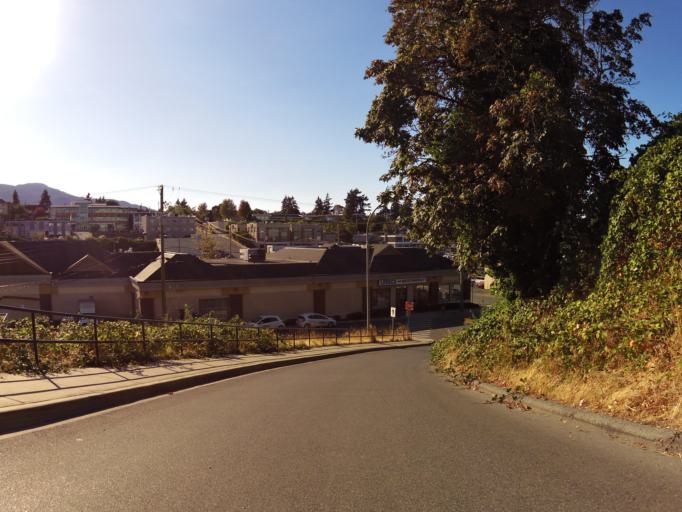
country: CA
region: British Columbia
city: Nanaimo
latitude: 49.1682
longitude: -123.9389
